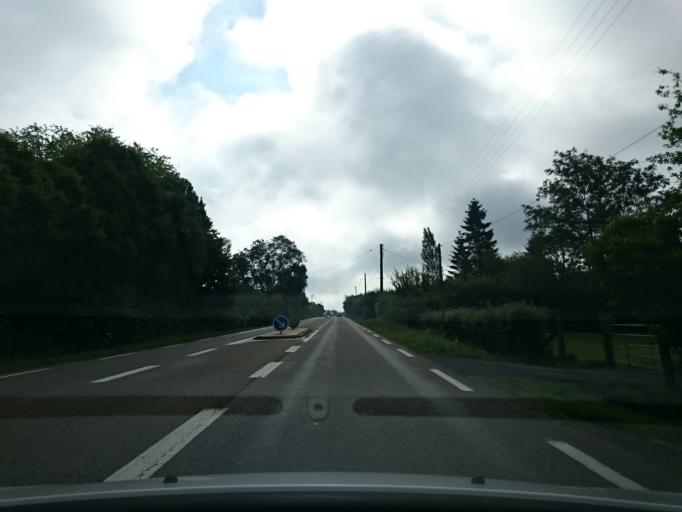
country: FR
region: Lower Normandy
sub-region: Departement du Calvados
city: Saint-Desir
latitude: 49.1351
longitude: 0.1429
